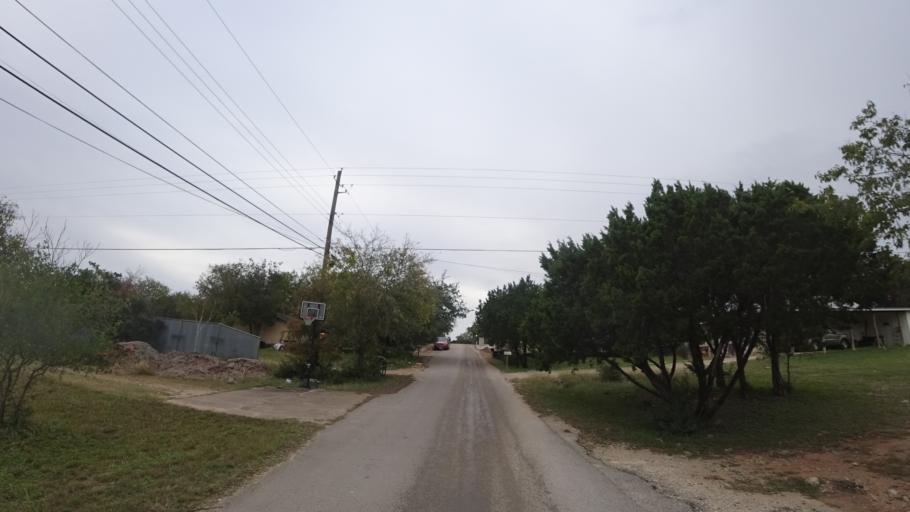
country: US
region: Texas
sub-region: Travis County
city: Hudson Bend
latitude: 30.3749
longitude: -97.9236
